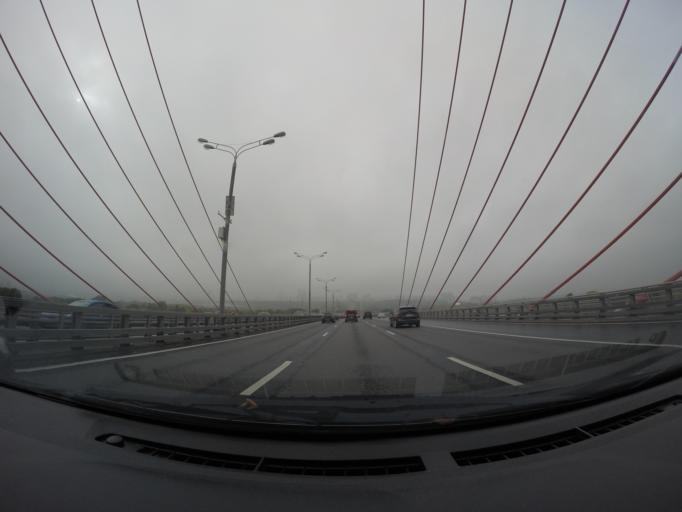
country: RU
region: Moscow
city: Shchukino
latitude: 55.7758
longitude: 37.4423
